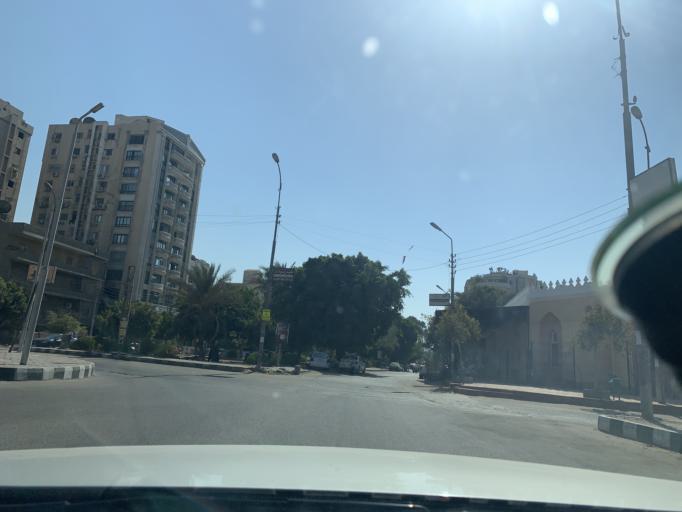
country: EG
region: Muhafazat al Qalyubiyah
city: Al Khankah
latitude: 30.1129
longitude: 31.3391
